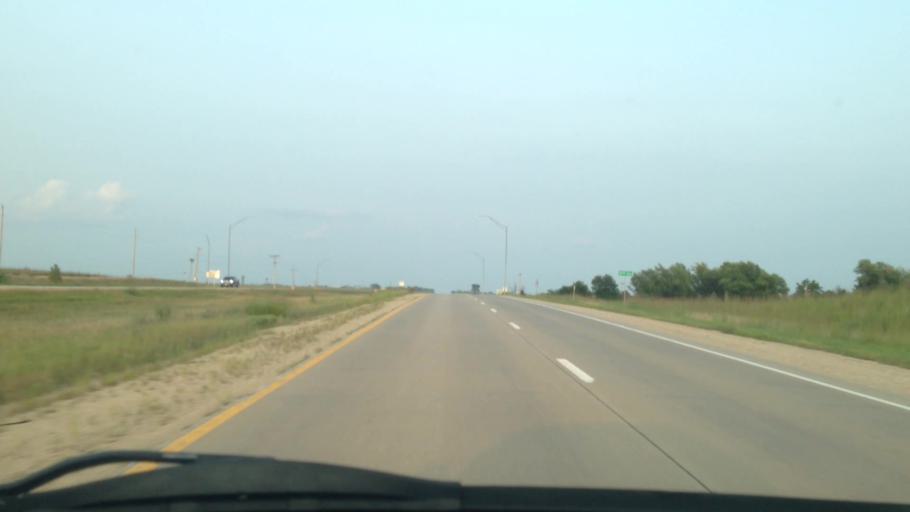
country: US
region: Iowa
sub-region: Benton County
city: Atkins
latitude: 41.9632
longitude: -91.9733
